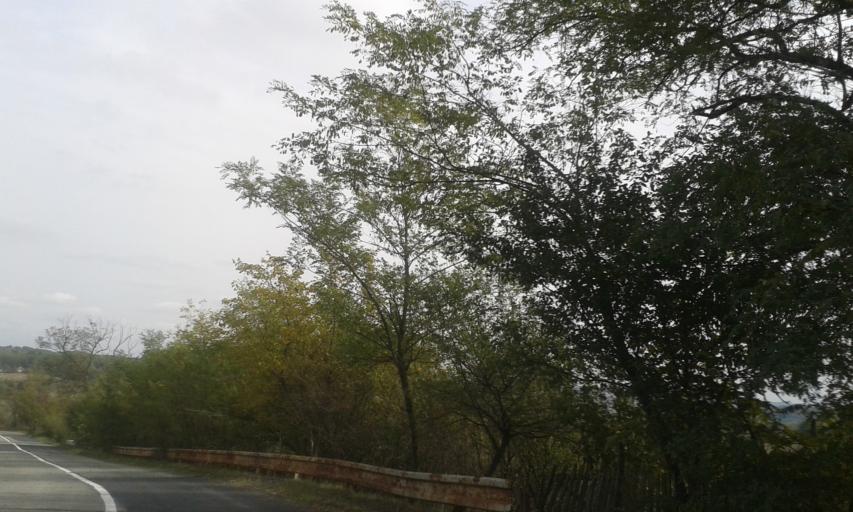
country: RO
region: Valcea
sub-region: Comuna Gradistea
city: Gradistea
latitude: 44.9149
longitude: 23.7740
